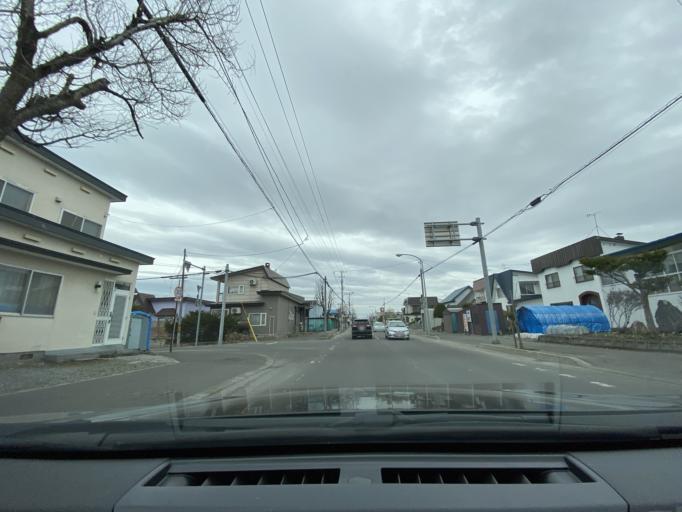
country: JP
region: Hokkaido
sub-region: Asahikawa-shi
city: Asahikawa
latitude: 43.7934
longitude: 142.4168
